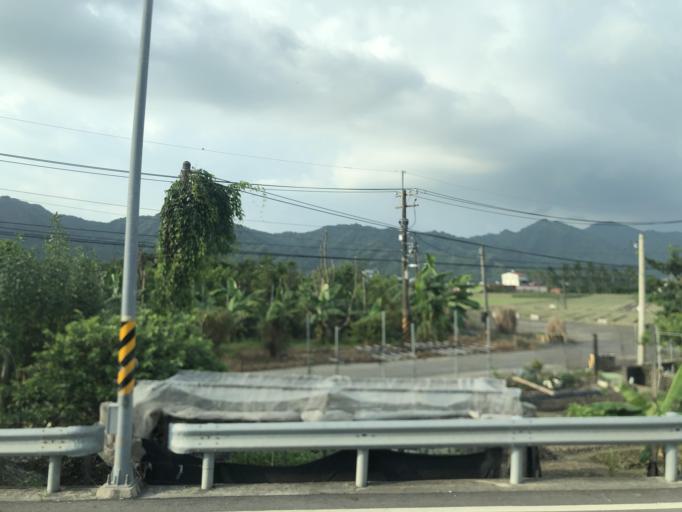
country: TW
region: Taiwan
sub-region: Pingtung
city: Pingtung
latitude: 22.8865
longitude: 120.5236
